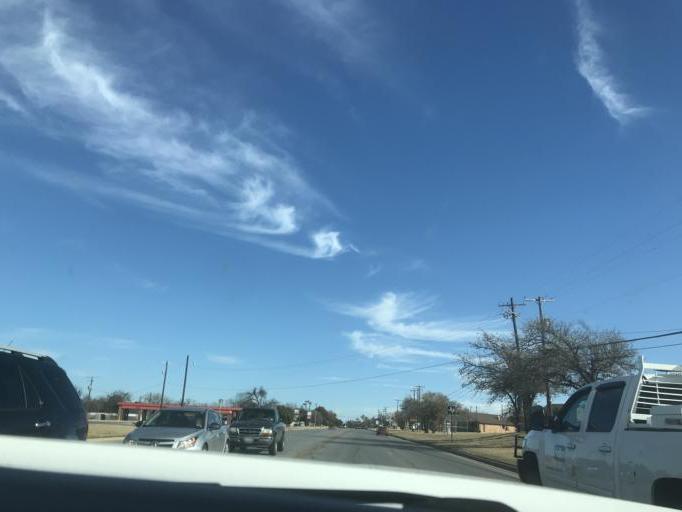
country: US
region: Texas
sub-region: Erath County
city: Stephenville
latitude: 32.2259
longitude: -98.2313
